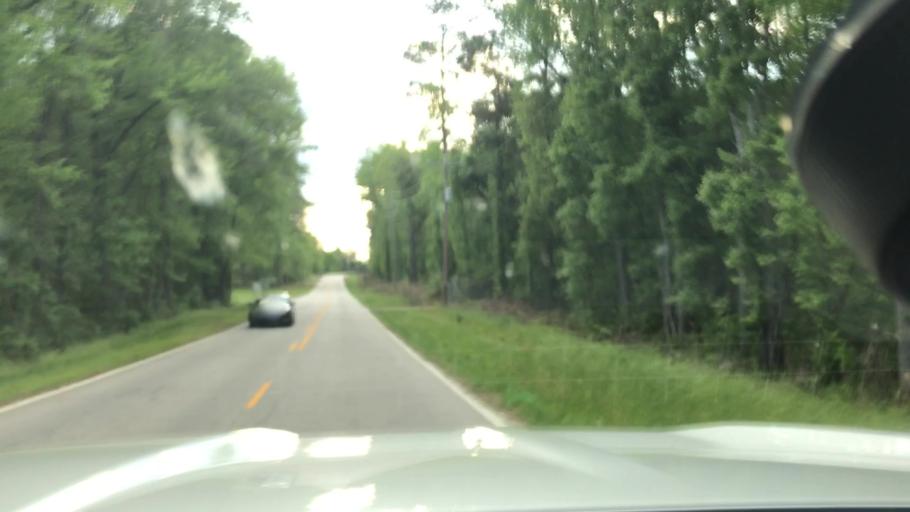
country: US
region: South Carolina
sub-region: Bamberg County
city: Denmark
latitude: 33.4521
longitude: -81.1314
